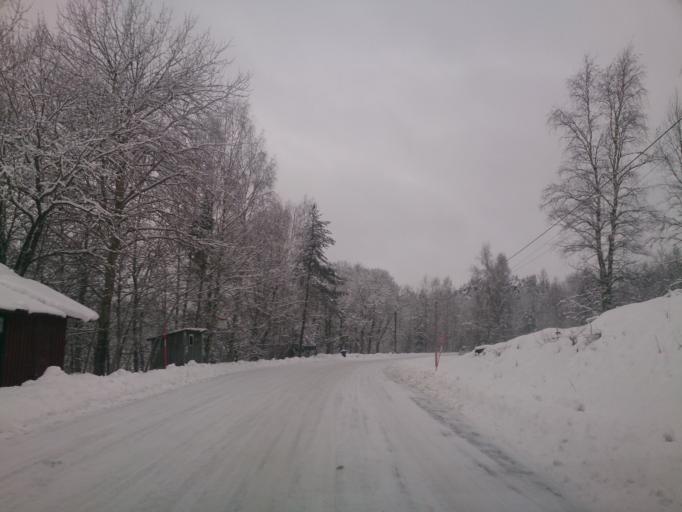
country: SE
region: OEstergoetland
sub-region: Atvidabergs Kommun
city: Atvidaberg
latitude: 58.2660
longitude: 16.0345
